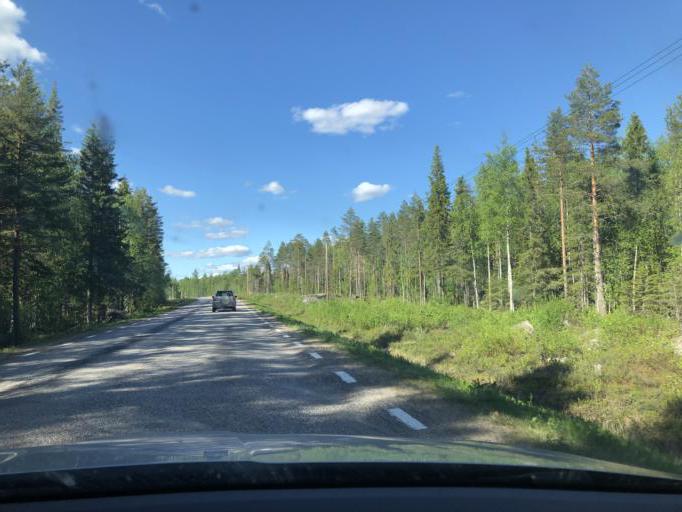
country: SE
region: Norrbotten
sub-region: Kalix Kommun
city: Kalix
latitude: 65.9343
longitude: 23.1605
